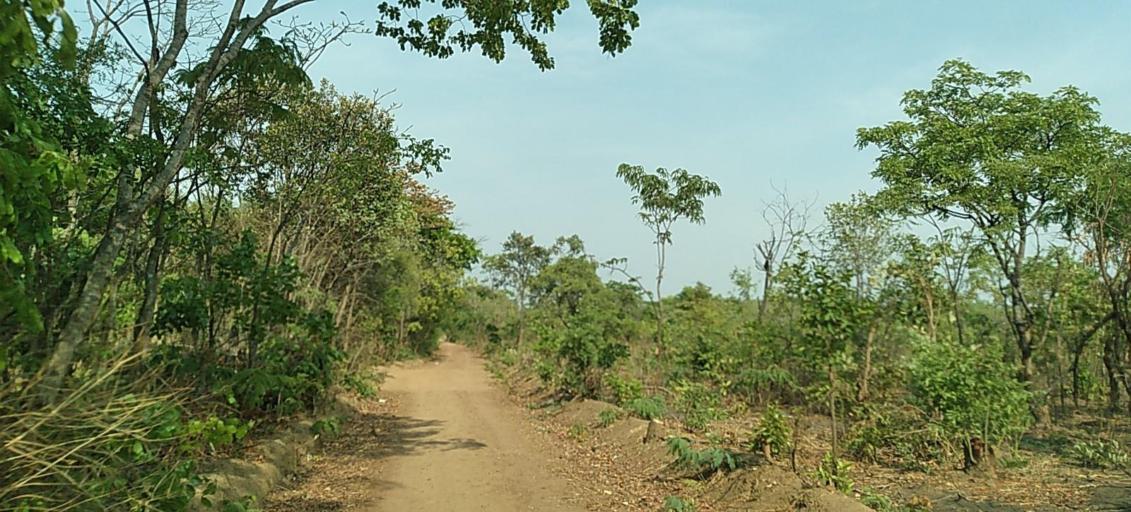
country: ZM
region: Copperbelt
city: Luanshya
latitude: -13.2204
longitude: 28.6634
